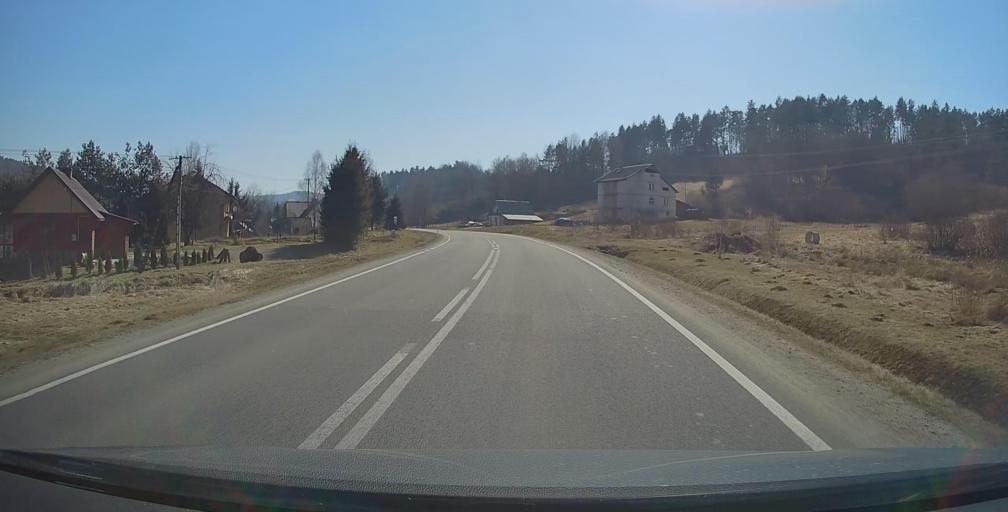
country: PL
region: Subcarpathian Voivodeship
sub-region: Powiat przemyski
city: Bircza
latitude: 49.6713
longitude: 22.4301
